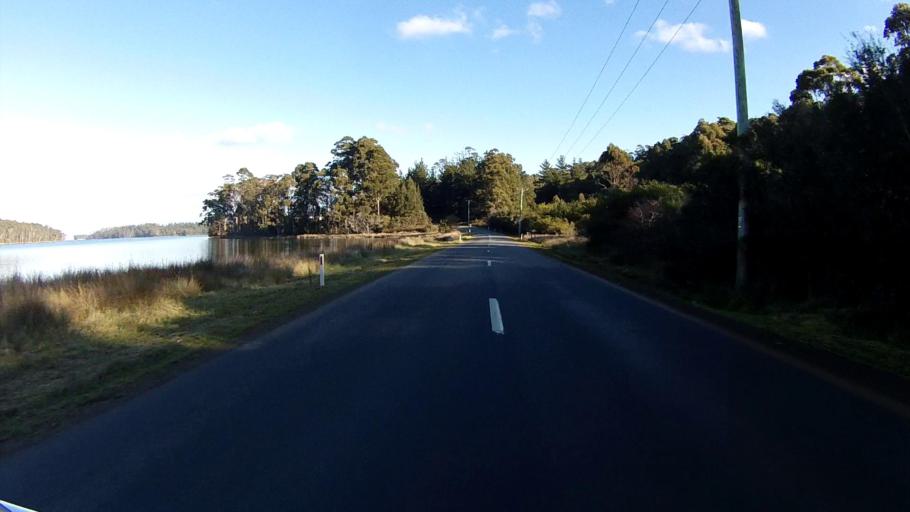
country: AU
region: Tasmania
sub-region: Clarence
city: Sandford
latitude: -43.1086
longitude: 147.8609
